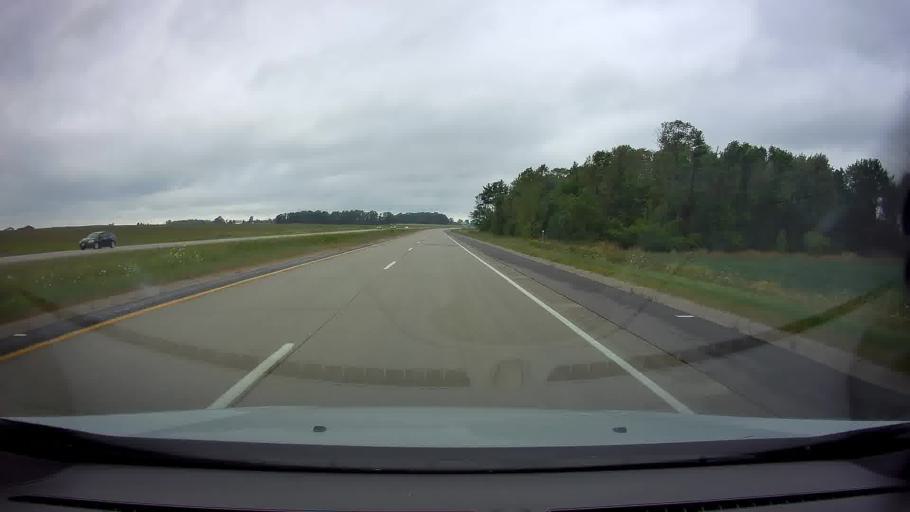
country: US
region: Wisconsin
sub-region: Brown County
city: Pulaski
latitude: 44.6529
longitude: -88.2985
